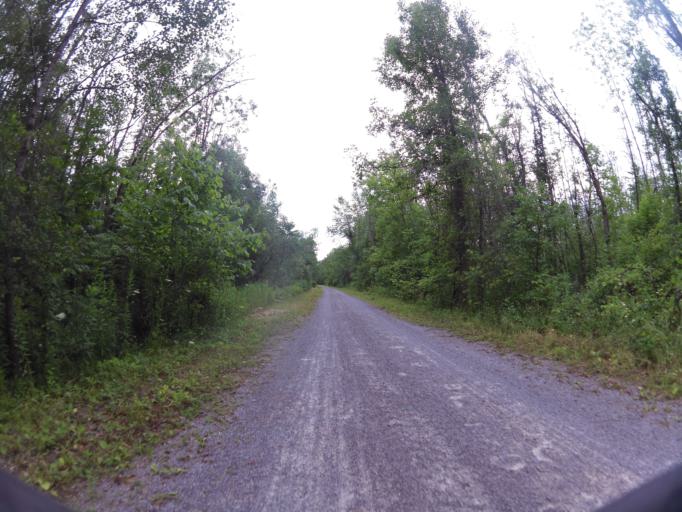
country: CA
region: Ontario
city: Ottawa
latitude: 45.2078
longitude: -75.6250
